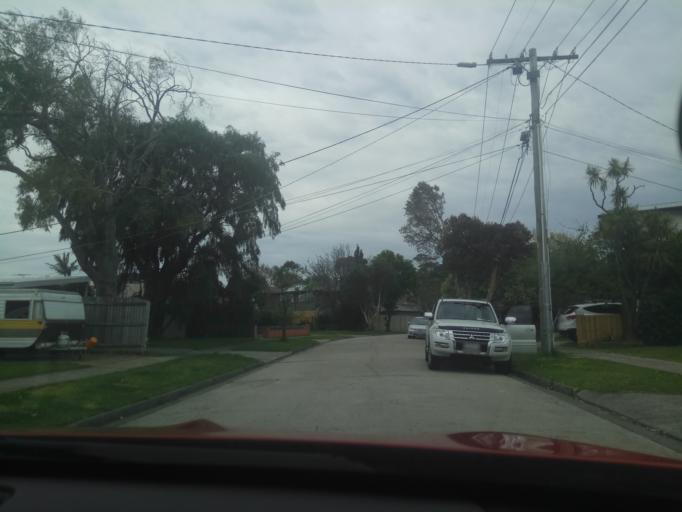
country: AU
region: Victoria
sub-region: Kingston
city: Aspendale
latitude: -38.0259
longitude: 145.1089
